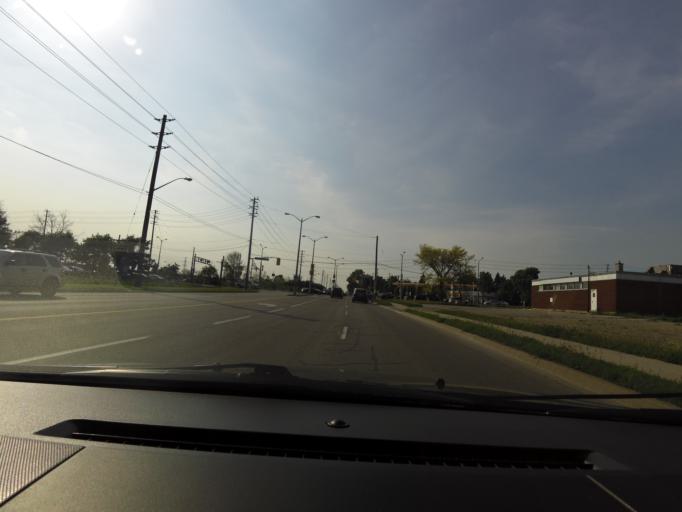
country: CA
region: Ontario
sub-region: Wellington County
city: Guelph
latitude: 43.5510
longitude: -80.2769
